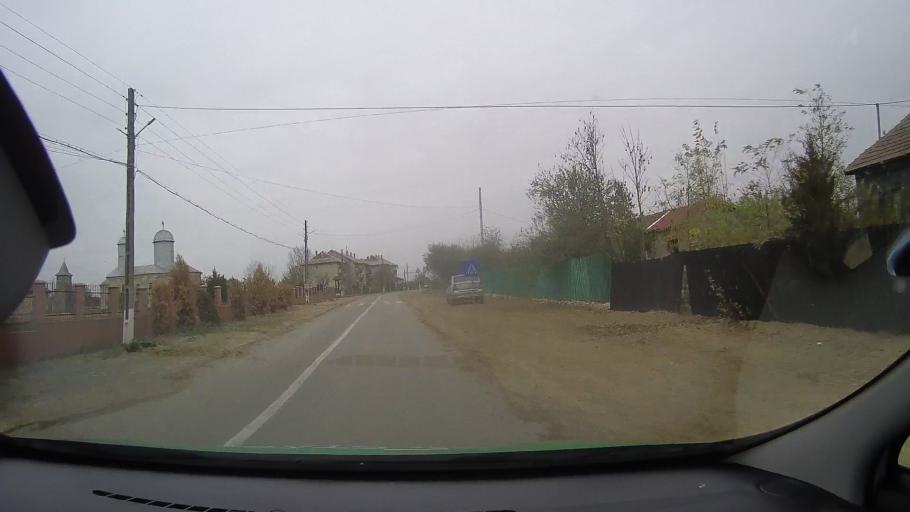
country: RO
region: Constanta
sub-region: Comuna Vulturu
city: Vulturu
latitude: 44.6473
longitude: 28.2699
